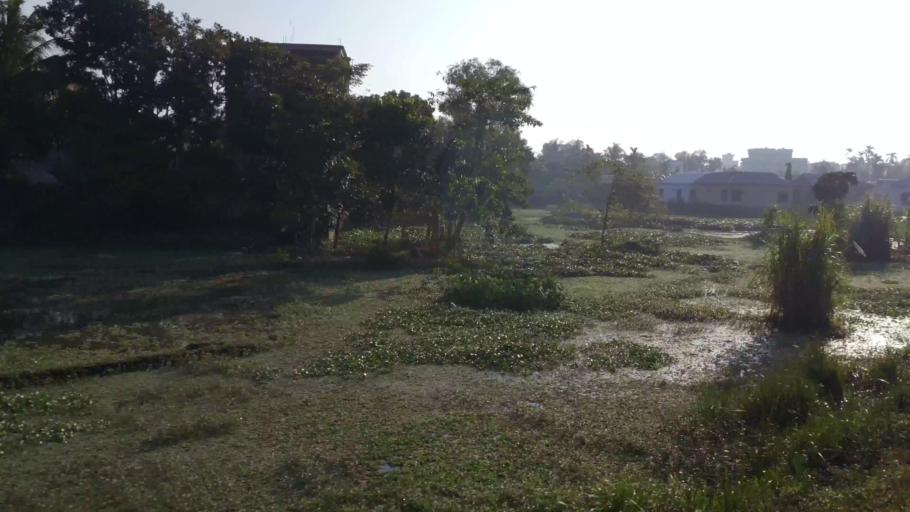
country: BD
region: Dhaka
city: Jamalpur
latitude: 24.8953
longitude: 89.9847
